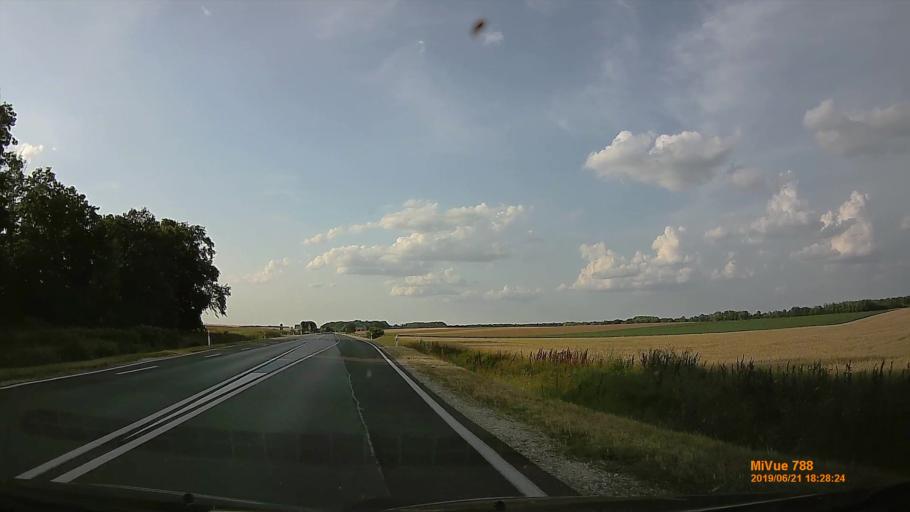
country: HU
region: Tolna
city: Madocsa
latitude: 46.7244
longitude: 18.8842
